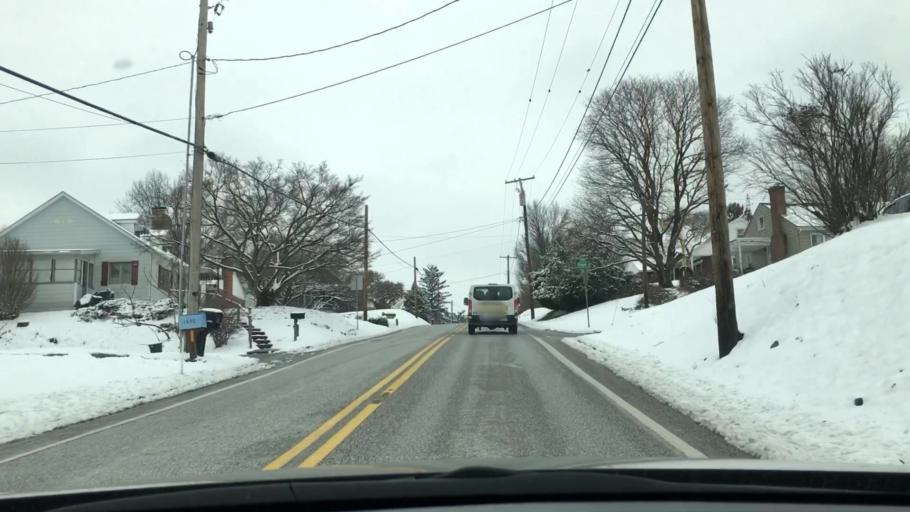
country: US
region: Pennsylvania
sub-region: York County
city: East York
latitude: 39.9861
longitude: -76.7069
